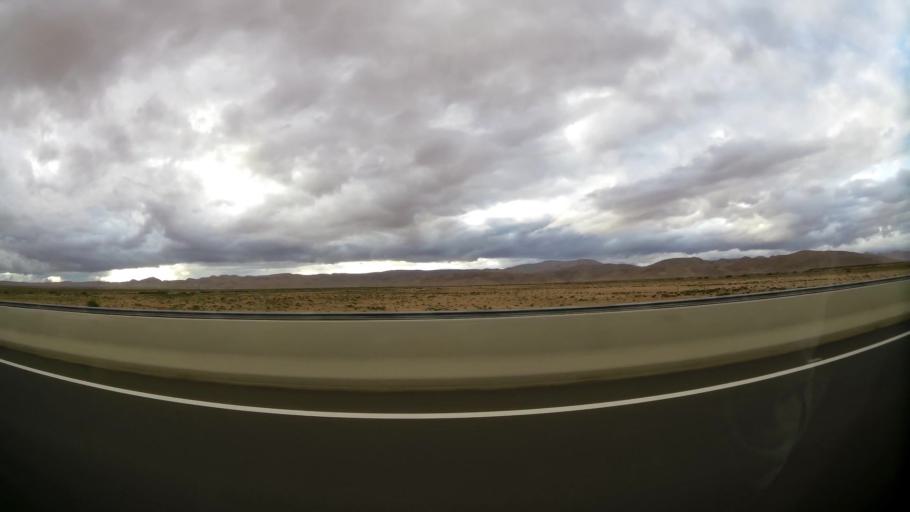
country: MA
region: Taza-Al Hoceima-Taounate
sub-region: Taza
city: Guercif
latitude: 34.3192
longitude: -3.5814
